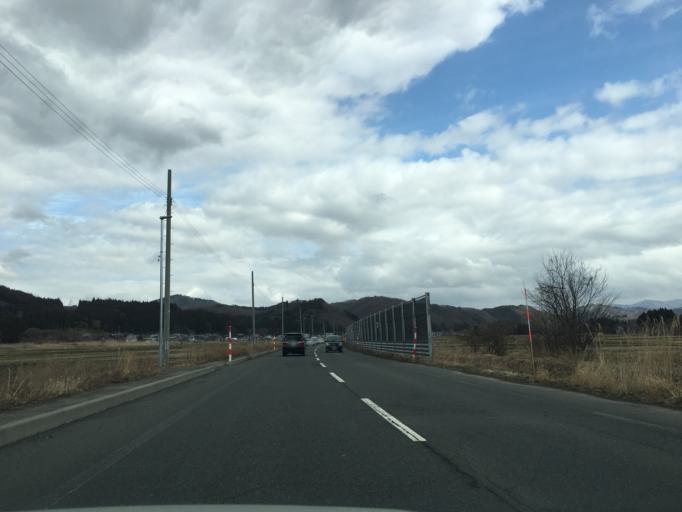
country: JP
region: Akita
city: Hanawa
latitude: 40.2316
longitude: 140.6845
